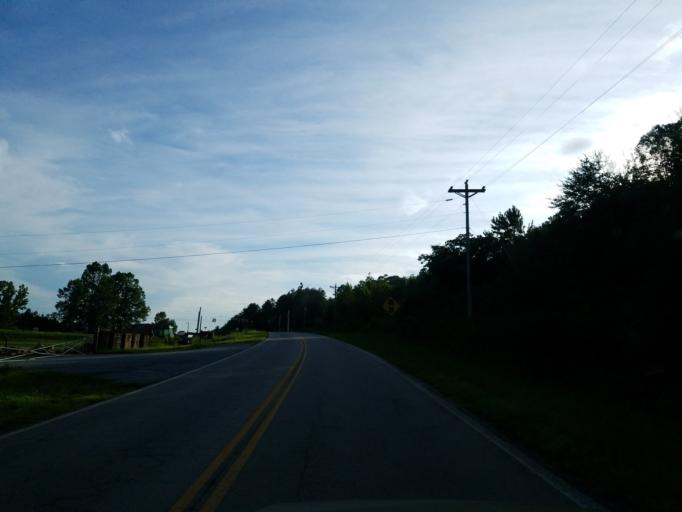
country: US
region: Georgia
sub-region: Lumpkin County
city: Dahlonega
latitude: 34.5231
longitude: -83.9134
